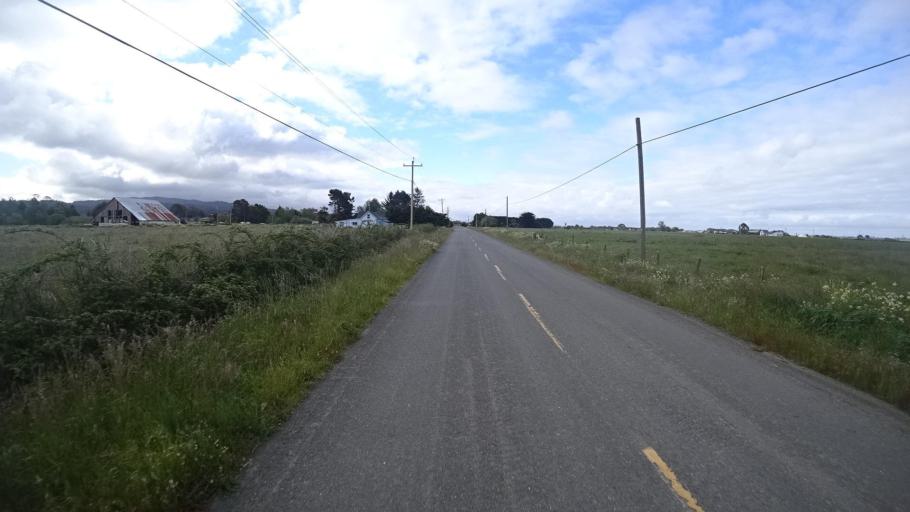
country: US
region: California
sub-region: Humboldt County
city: Arcata
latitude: 40.9061
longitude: -124.0914
